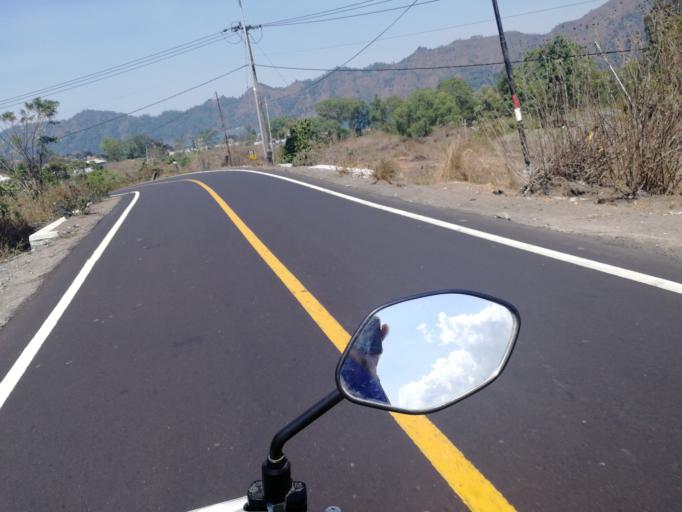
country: ID
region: Bali
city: Banjar Trunyan
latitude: -8.2535
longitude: 115.3967
